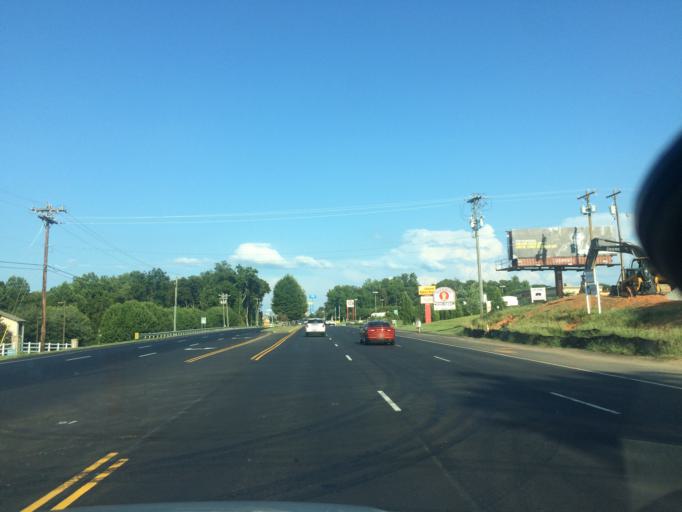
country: US
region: South Carolina
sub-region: Spartanburg County
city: Fairforest
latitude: 34.9360
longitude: -82.0121
